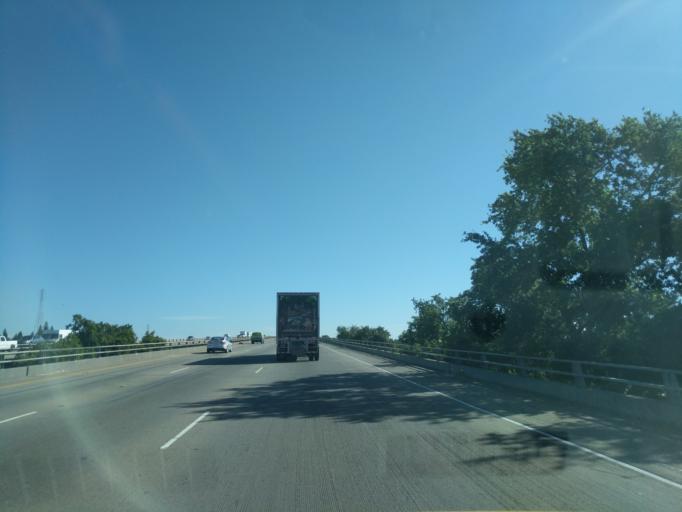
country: US
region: California
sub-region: Yolo County
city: West Sacramento
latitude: 38.5931
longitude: -121.5511
